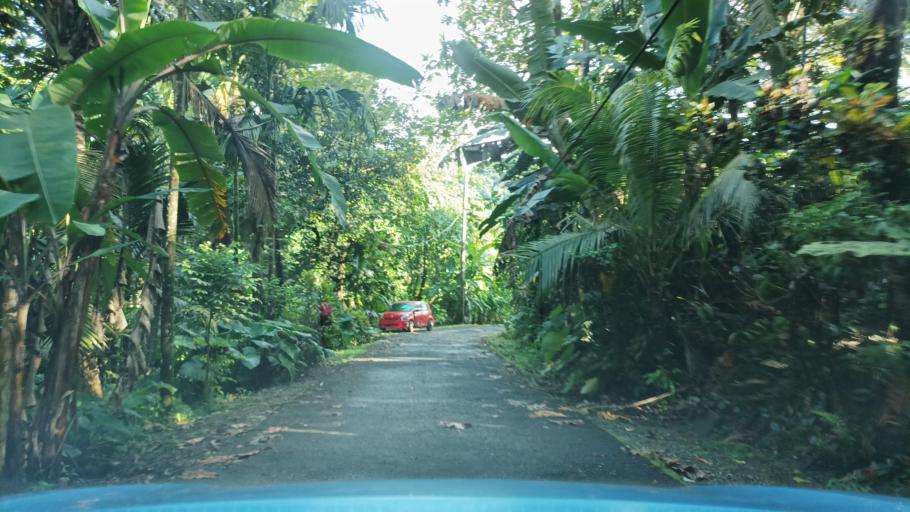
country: FM
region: Pohnpei
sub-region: Kolonia Municipality
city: Kolonia Town
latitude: 6.9611
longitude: 158.1953
